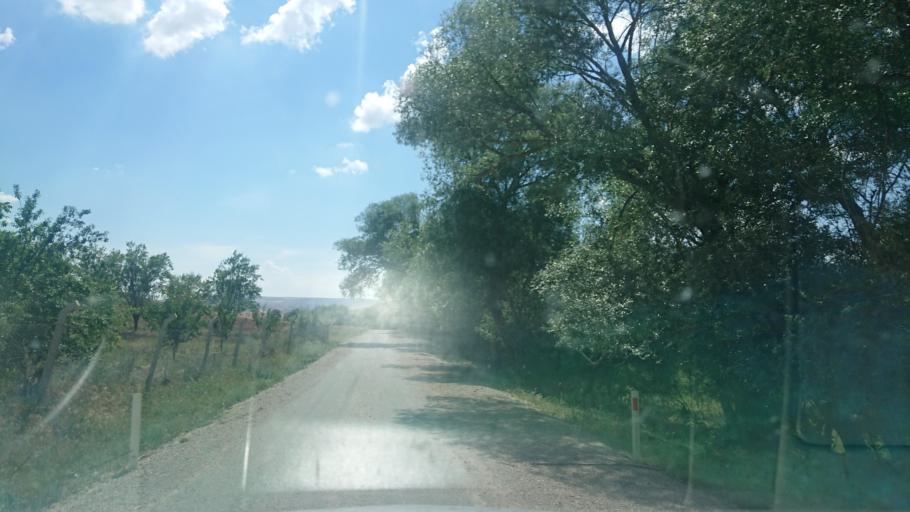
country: TR
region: Aksaray
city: Agacoren
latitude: 38.8369
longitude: 33.8074
